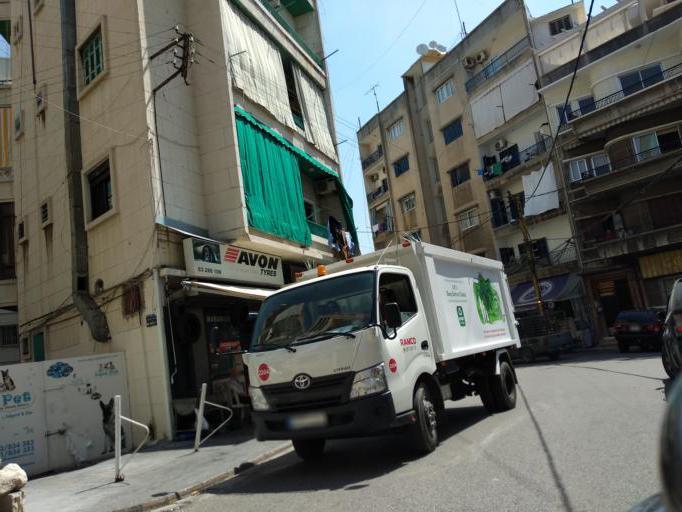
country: LB
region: Mont-Liban
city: Jdaidet el Matn
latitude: 33.8923
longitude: 35.5311
